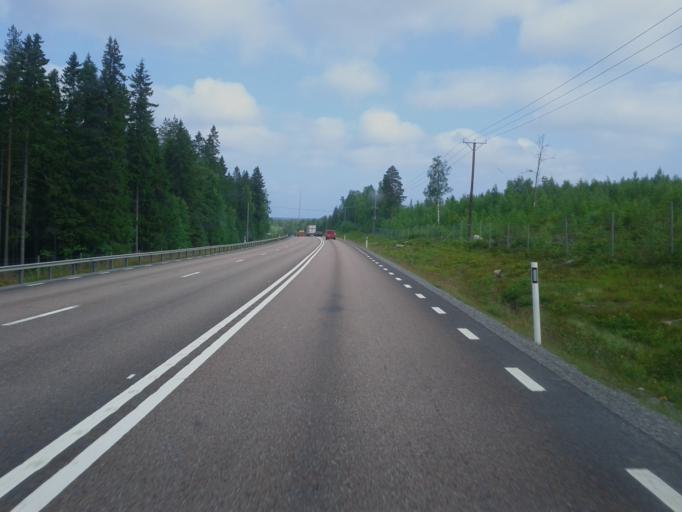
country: SE
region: Vaesterbotten
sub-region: Skelleftea Kommun
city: Burea
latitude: 64.4590
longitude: 21.2895
